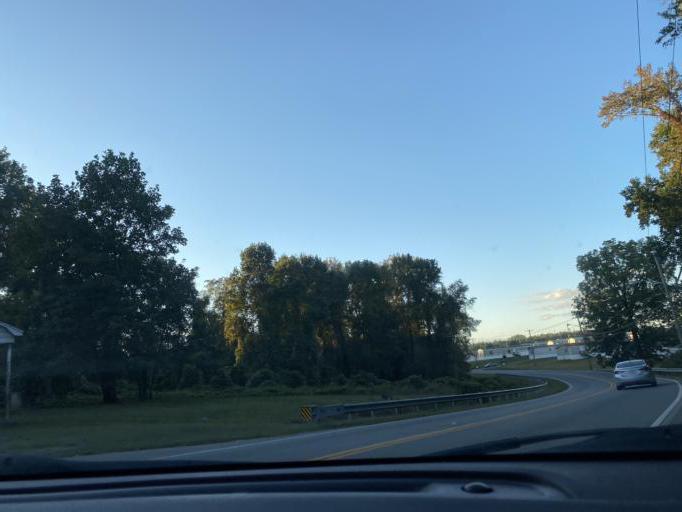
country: US
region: South Carolina
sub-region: Cherokee County
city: East Gaffney
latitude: 35.0869
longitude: -81.6457
